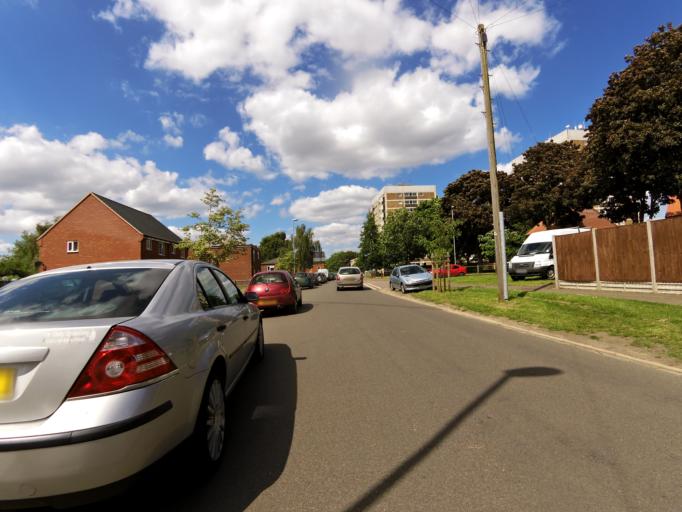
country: GB
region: England
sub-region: Norfolk
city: Norwich
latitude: 52.6498
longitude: 1.2696
